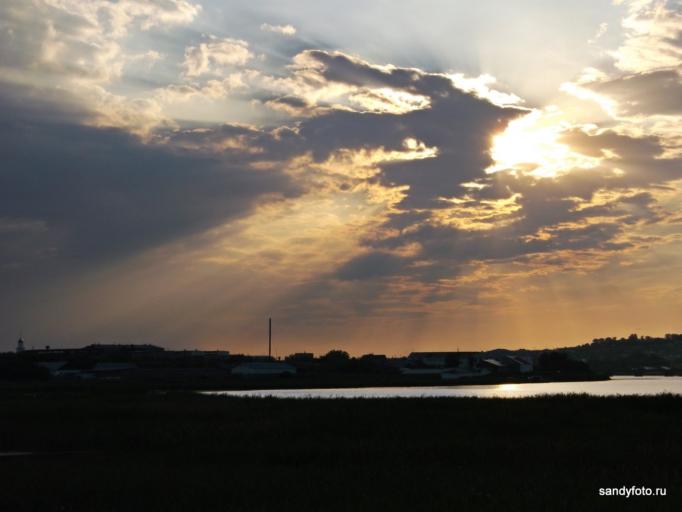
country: RU
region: Chelyabinsk
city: Troitsk
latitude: 54.0850
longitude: 61.5934
